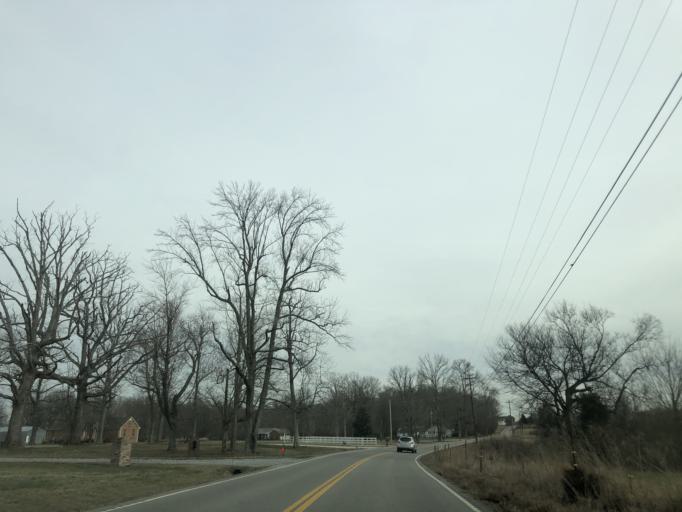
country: US
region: Tennessee
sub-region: Sumner County
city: White House
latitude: 36.4876
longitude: -86.5841
